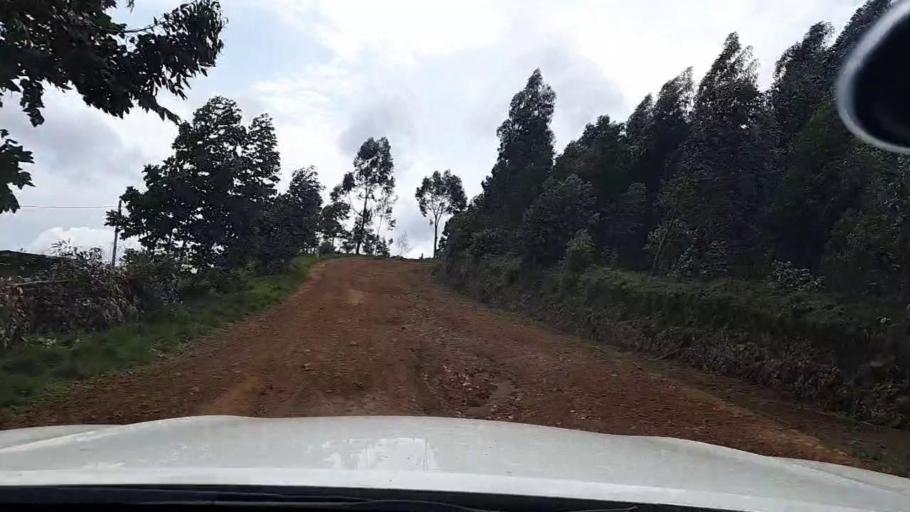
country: RW
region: Western Province
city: Kibuye
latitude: -2.1312
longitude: 29.3773
